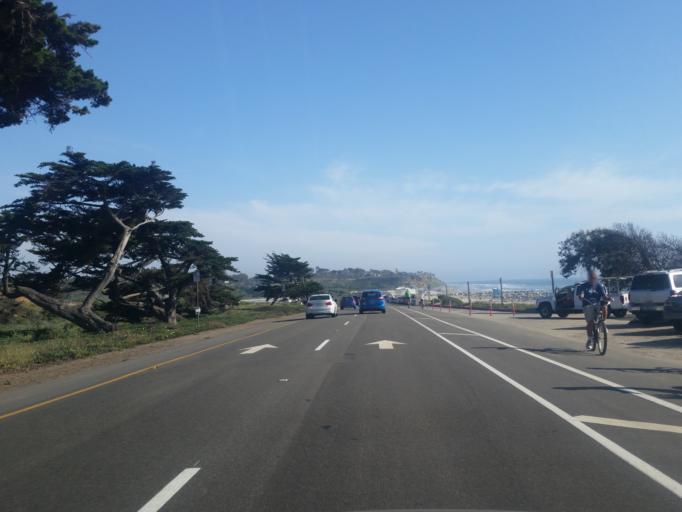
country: US
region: California
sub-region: San Diego County
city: Encinitas
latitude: 33.0911
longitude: -117.3141
